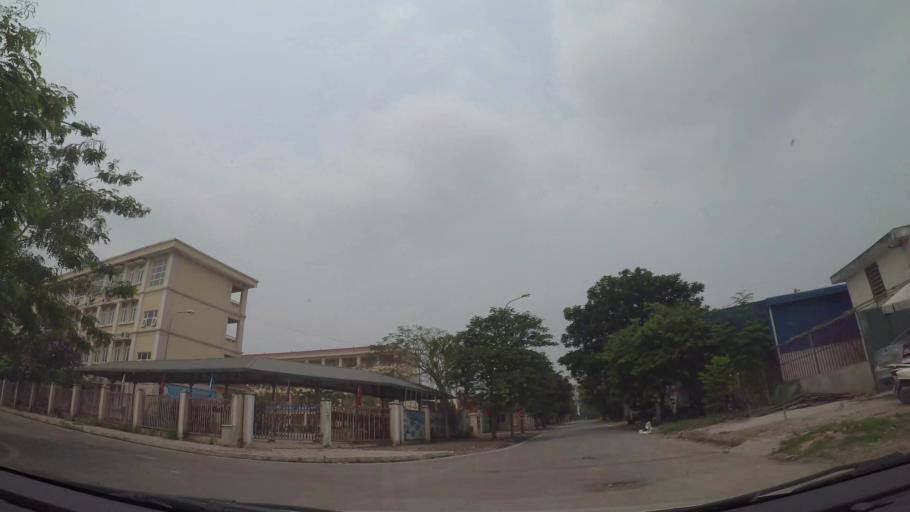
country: VN
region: Ha Noi
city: Cau Dien
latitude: 21.0296
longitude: 105.7478
